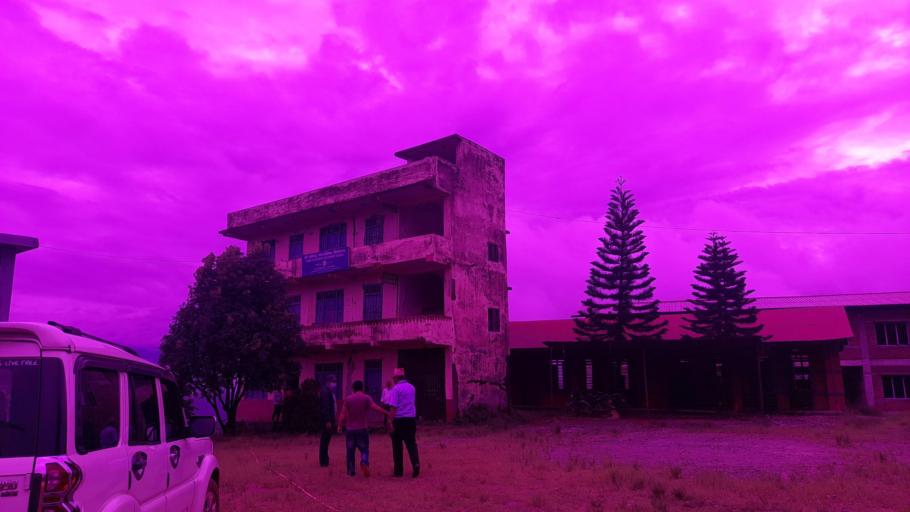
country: NP
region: Central Region
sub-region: Bagmati Zone
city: Kathmandu
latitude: 27.8696
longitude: 85.2146
